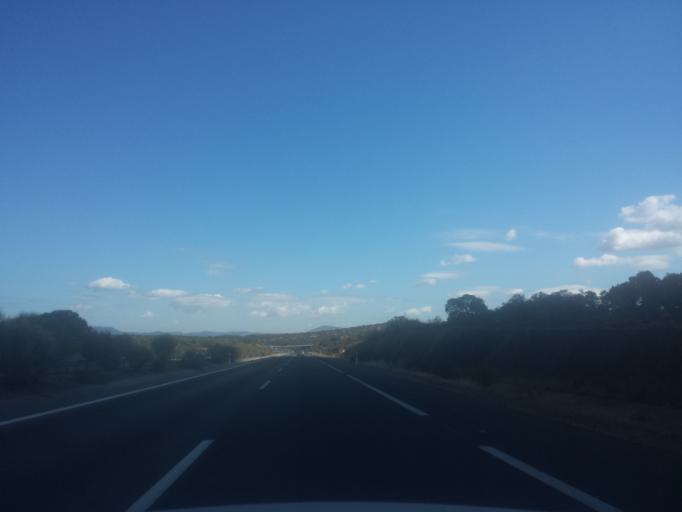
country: ES
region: Andalusia
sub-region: Provincia de Huelva
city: Santa Olalla del Cala
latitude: 37.8496
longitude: -6.2189
